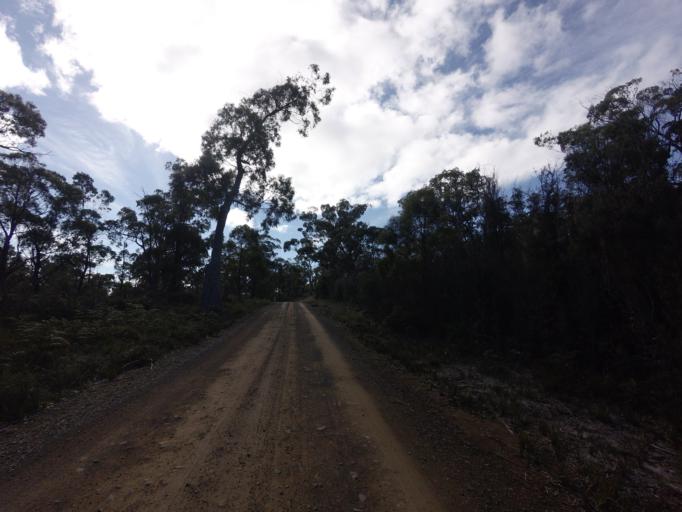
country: AU
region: Tasmania
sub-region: Clarence
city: Sandford
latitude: -42.9832
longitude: 147.7130
